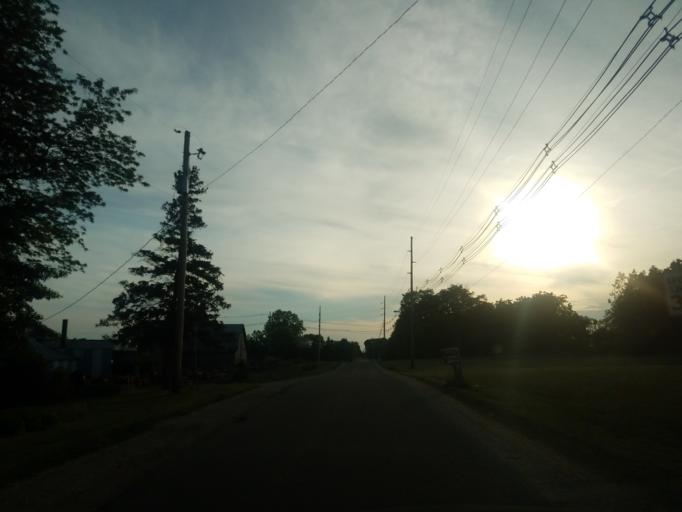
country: US
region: Illinois
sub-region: McLean County
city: Bloomington
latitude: 40.4444
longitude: -89.0058
